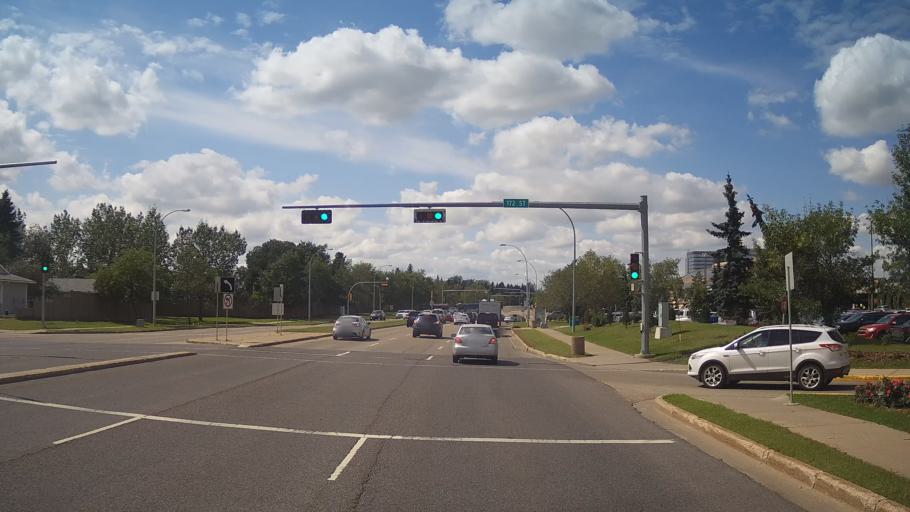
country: CA
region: Alberta
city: St. Albert
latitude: 53.5196
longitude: -113.6181
